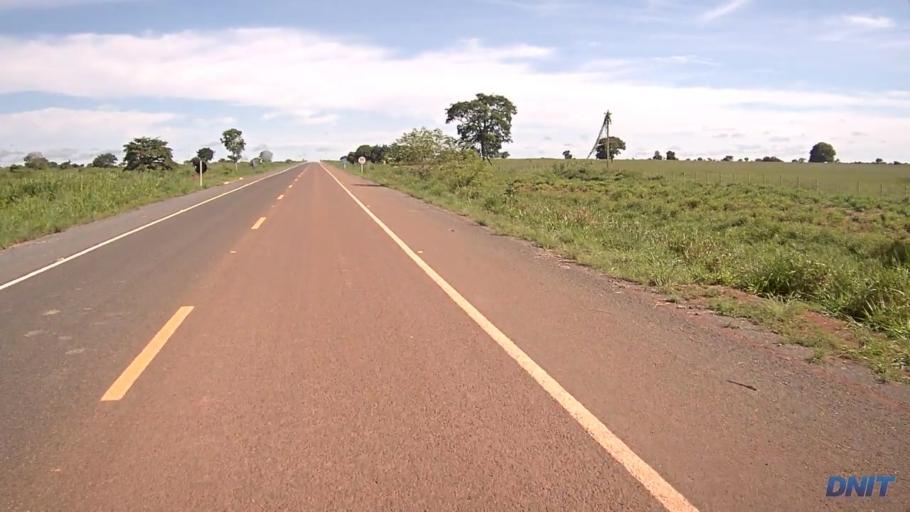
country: BR
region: Goias
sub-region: Sao Miguel Do Araguaia
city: Sao Miguel do Araguaia
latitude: -13.4957
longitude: -50.1076
